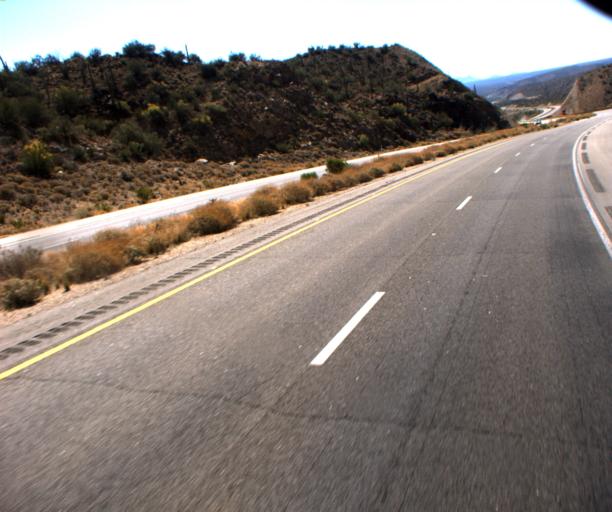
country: US
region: Arizona
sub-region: Yavapai County
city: Bagdad
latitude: 34.4092
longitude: -113.2269
